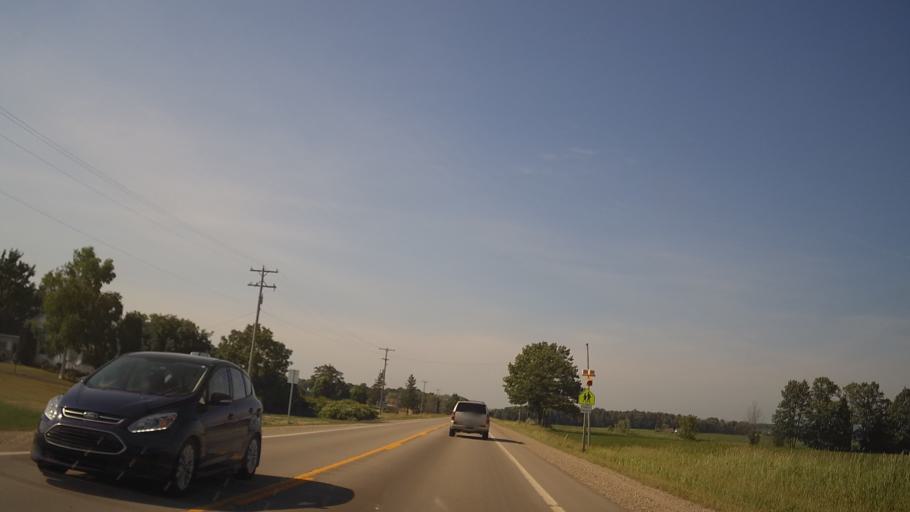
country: US
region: Michigan
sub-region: Ogemaw County
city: West Branch
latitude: 44.3042
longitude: -84.1258
